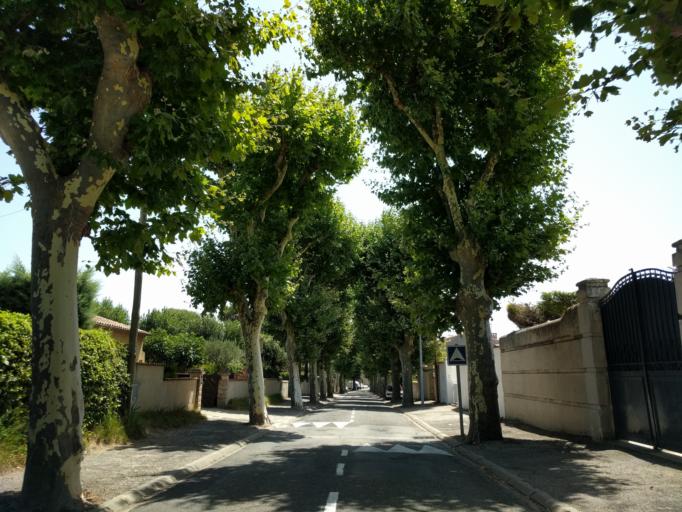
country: FR
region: Languedoc-Roussillon
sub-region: Departement de l'Aude
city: Palaja
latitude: 43.2023
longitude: 2.3934
